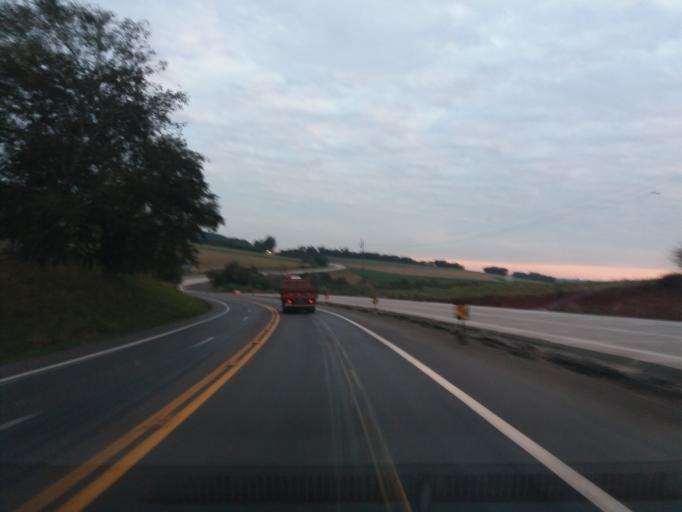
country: BR
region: Parana
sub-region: Realeza
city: Realeza
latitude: -25.3819
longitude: -53.5770
